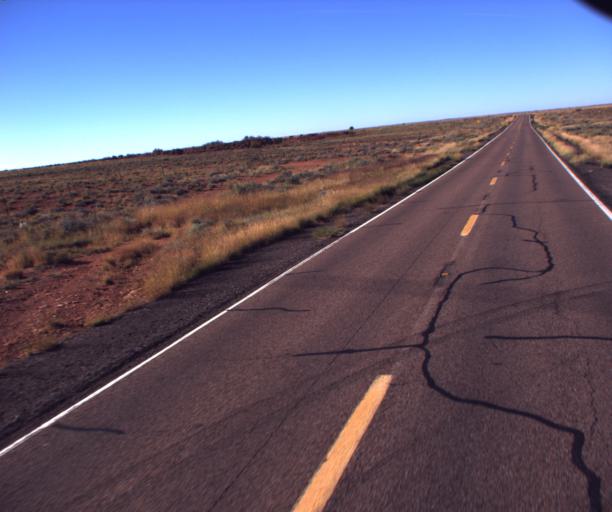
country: US
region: Arizona
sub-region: Navajo County
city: Holbrook
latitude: 34.7939
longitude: -110.2164
